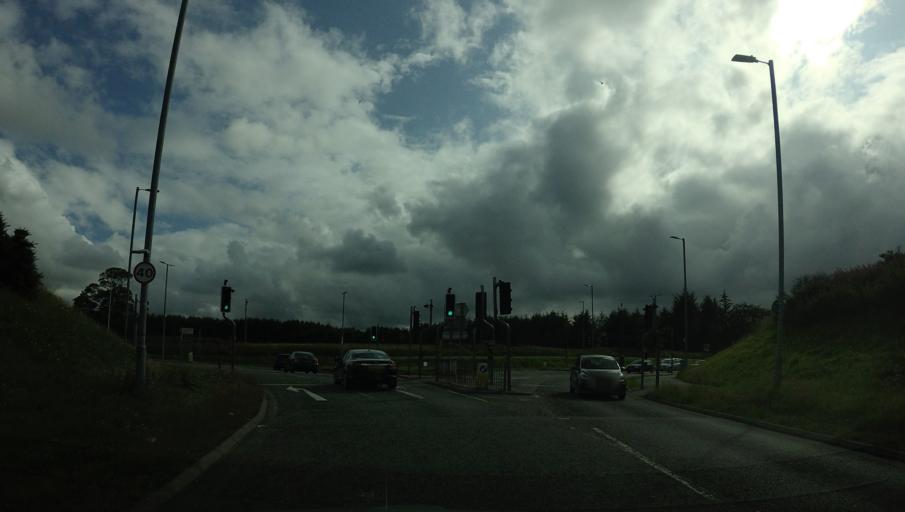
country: GB
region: Scotland
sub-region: Aberdeen City
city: Cults
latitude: 57.1463
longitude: -2.2024
